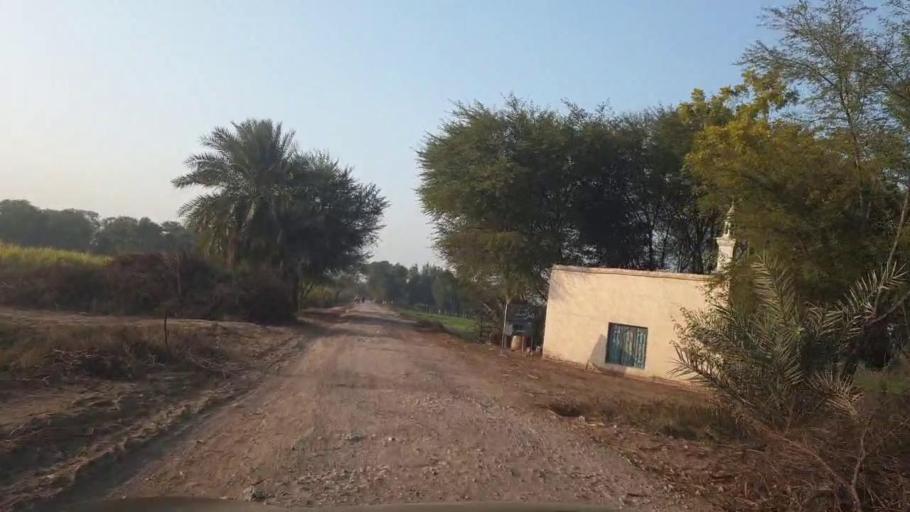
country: PK
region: Sindh
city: Ubauro
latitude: 28.3169
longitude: 69.7780
